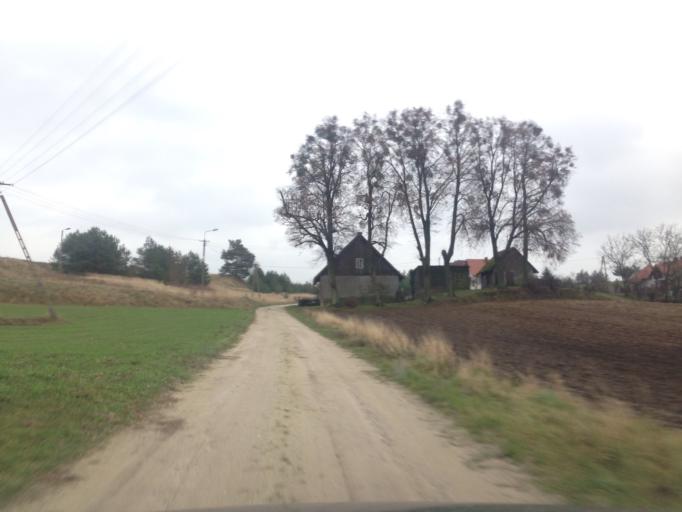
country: PL
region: Kujawsko-Pomorskie
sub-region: Powiat brodnicki
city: Gorzno
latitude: 53.2098
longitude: 19.6694
